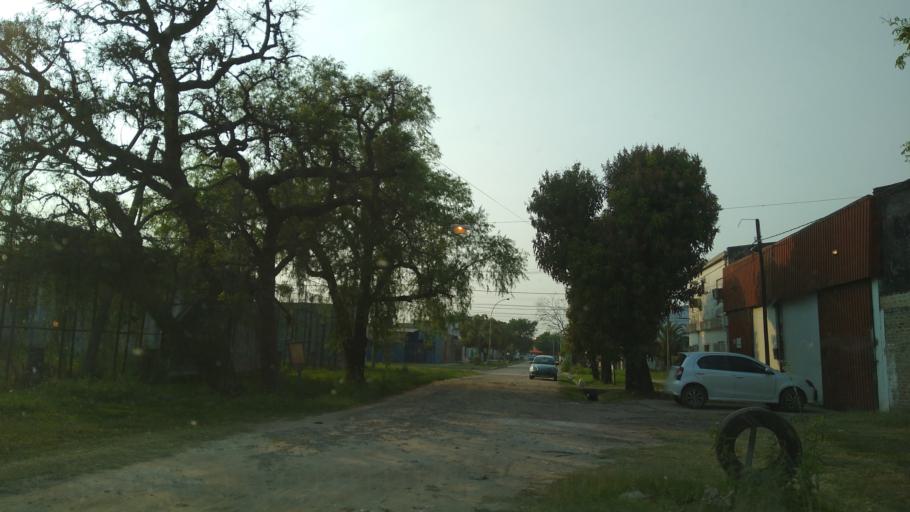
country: AR
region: Chaco
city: Barranqueras
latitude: -27.4812
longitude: -58.9404
